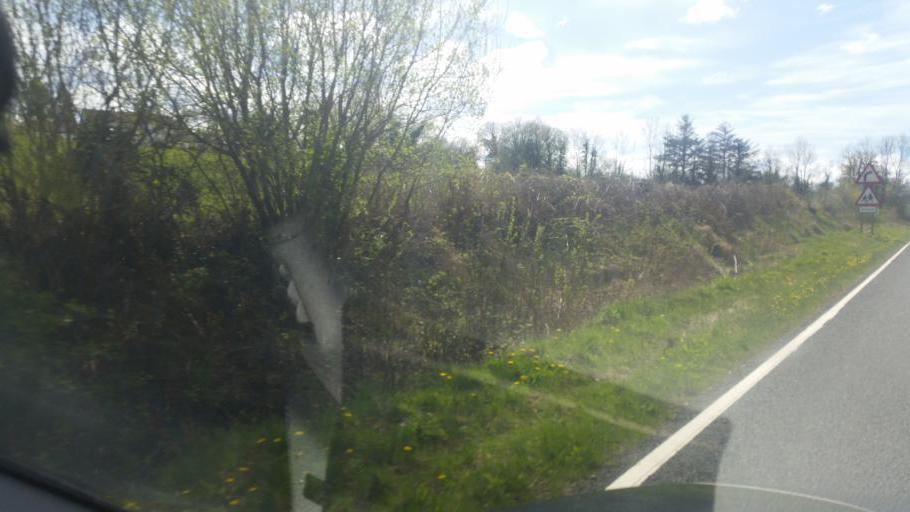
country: IE
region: Ulster
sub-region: County Donegal
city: Ballyshannon
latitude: 54.4674
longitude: -8.0352
